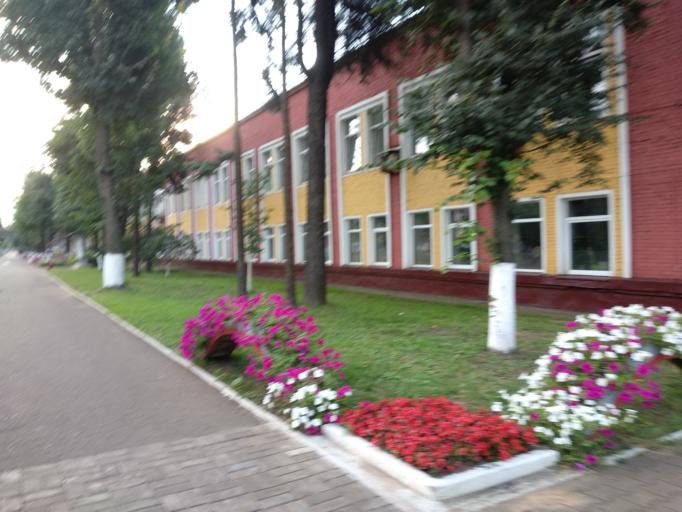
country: BY
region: Minsk
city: Minsk
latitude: 53.8911
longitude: 27.6197
